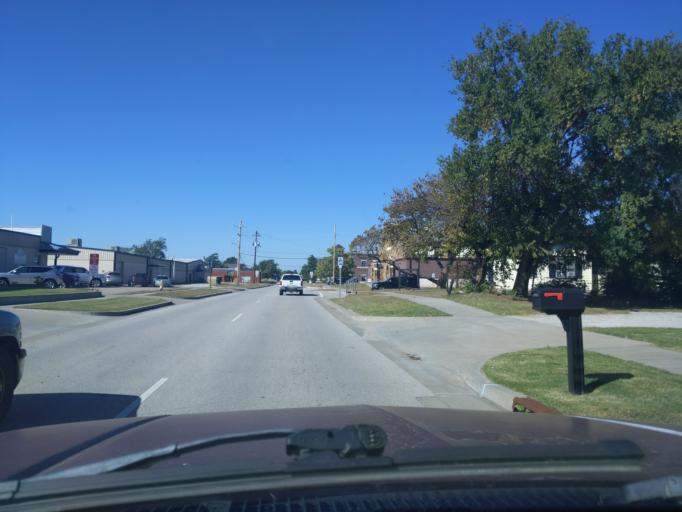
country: US
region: Oklahoma
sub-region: Tulsa County
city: Jenks
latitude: 36.0236
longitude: -95.9653
